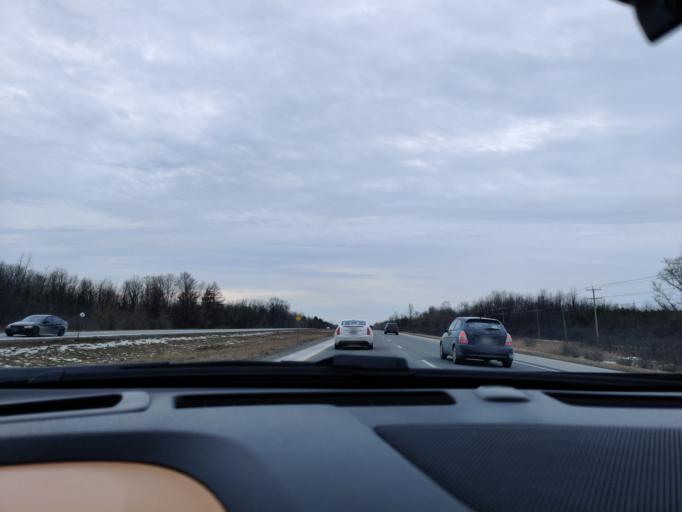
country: CA
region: Ontario
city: Prescott
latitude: 44.6783
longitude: -75.5960
